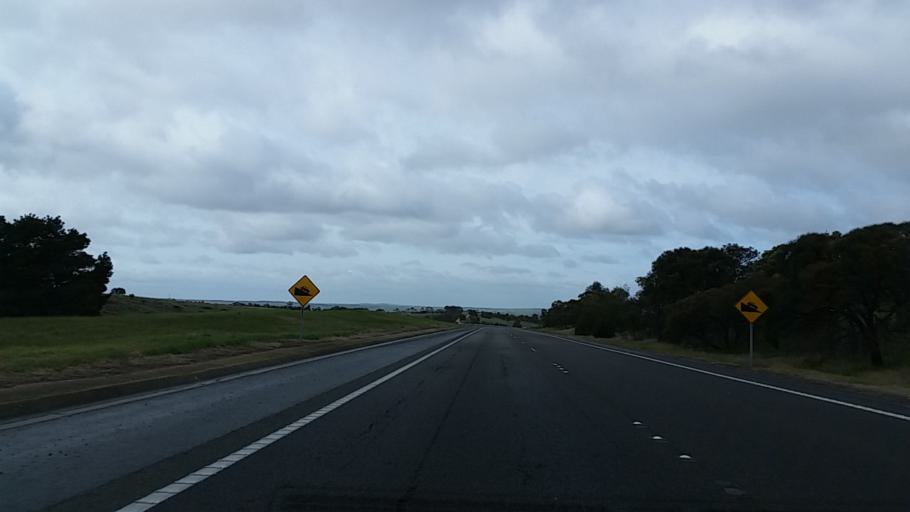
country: AU
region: South Australia
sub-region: Mount Barker
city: Callington
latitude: -35.0989
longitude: 138.9677
